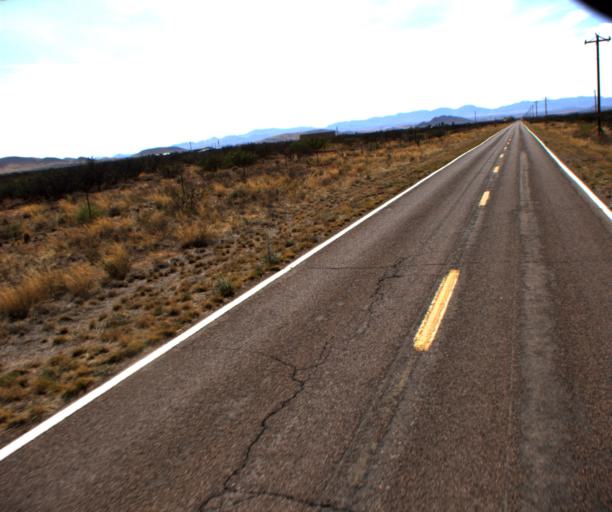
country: US
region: Arizona
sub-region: Cochise County
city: Willcox
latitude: 31.8761
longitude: -109.5552
